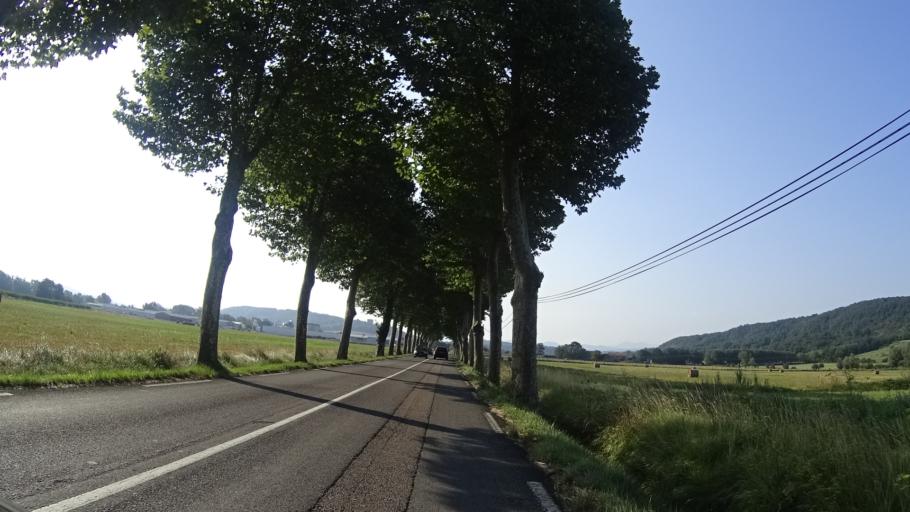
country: FR
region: Midi-Pyrenees
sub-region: Departement de l'Ariege
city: Mirepoix
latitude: 43.0510
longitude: 1.8889
